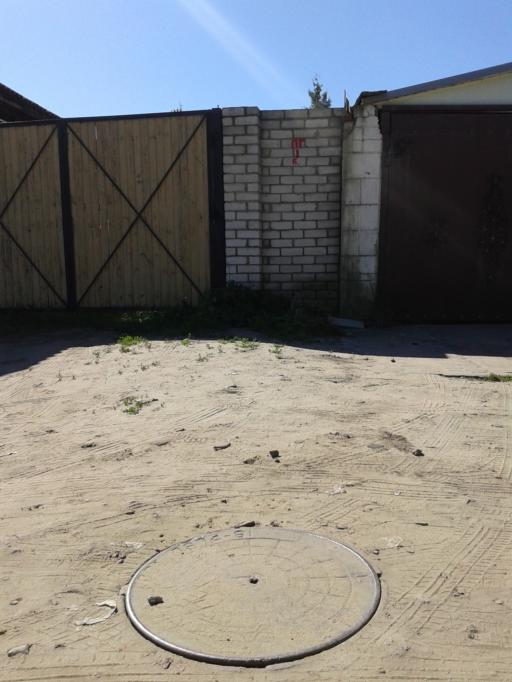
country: RU
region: Voronezj
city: Pridonskoy
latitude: 51.6612
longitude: 39.1210
